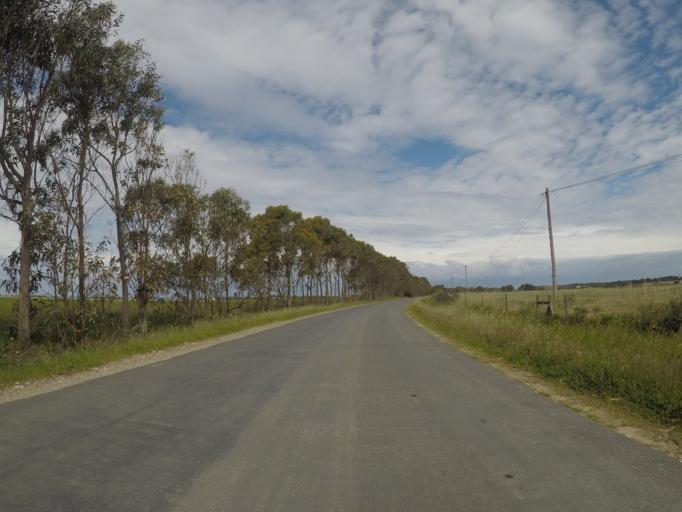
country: PT
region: Beja
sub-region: Odemira
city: Sao Teotonio
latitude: 37.4909
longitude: -8.7810
